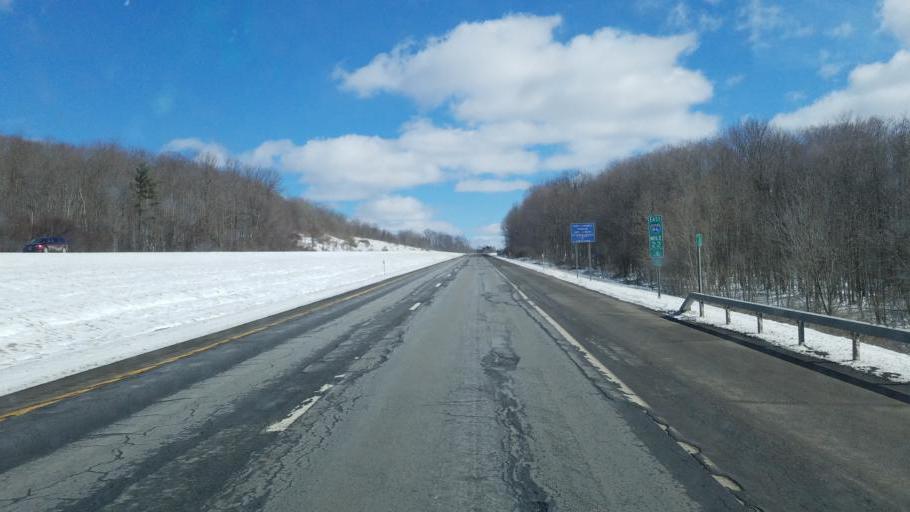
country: US
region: New York
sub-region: Chautauqua County
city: Lakewood
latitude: 42.1370
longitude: -79.3424
